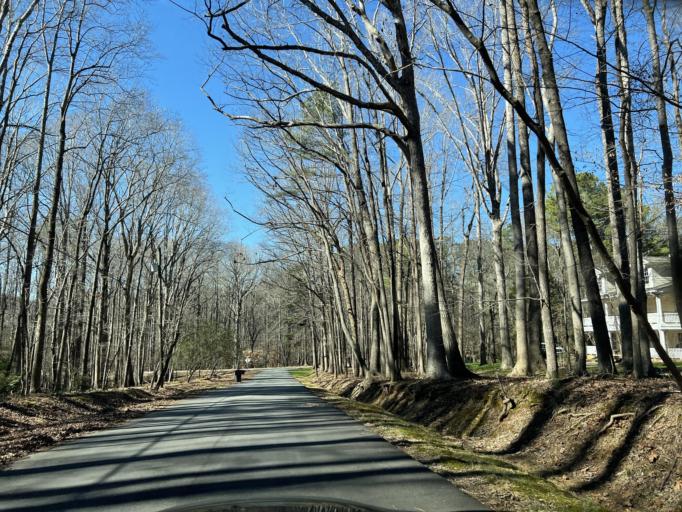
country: US
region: North Carolina
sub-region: Wake County
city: Wake Forest
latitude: 35.9077
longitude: -78.6116
